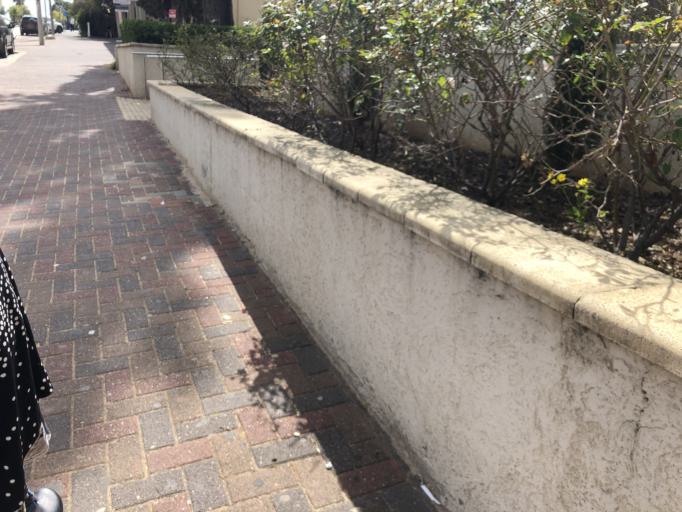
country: IL
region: Haifa
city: Hadera
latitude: 32.4760
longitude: 34.9721
